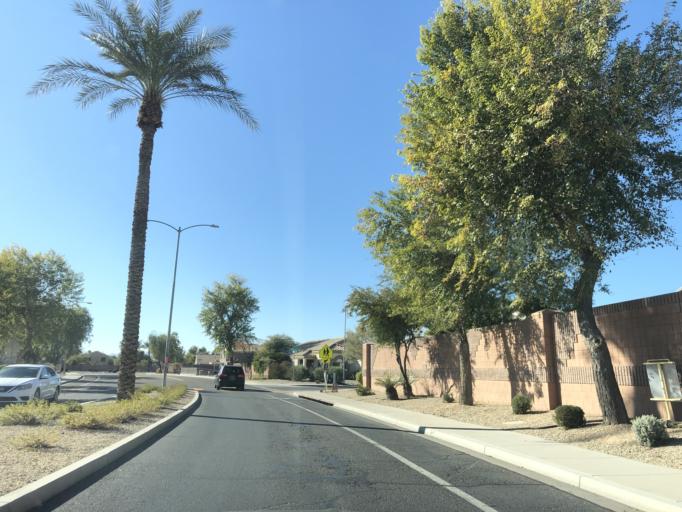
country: US
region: Arizona
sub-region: Maricopa County
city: El Mirage
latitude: 33.6168
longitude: -112.3338
